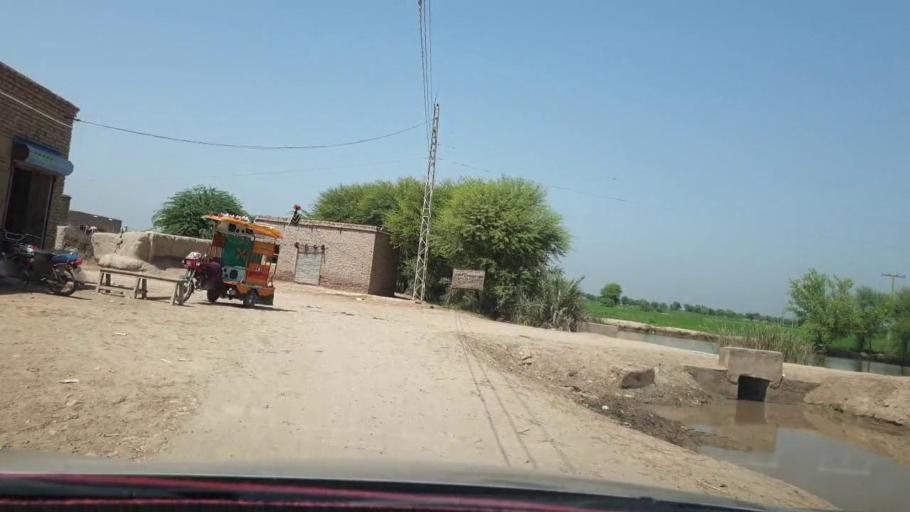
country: PK
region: Sindh
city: Warah
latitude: 27.5280
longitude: 67.8106
